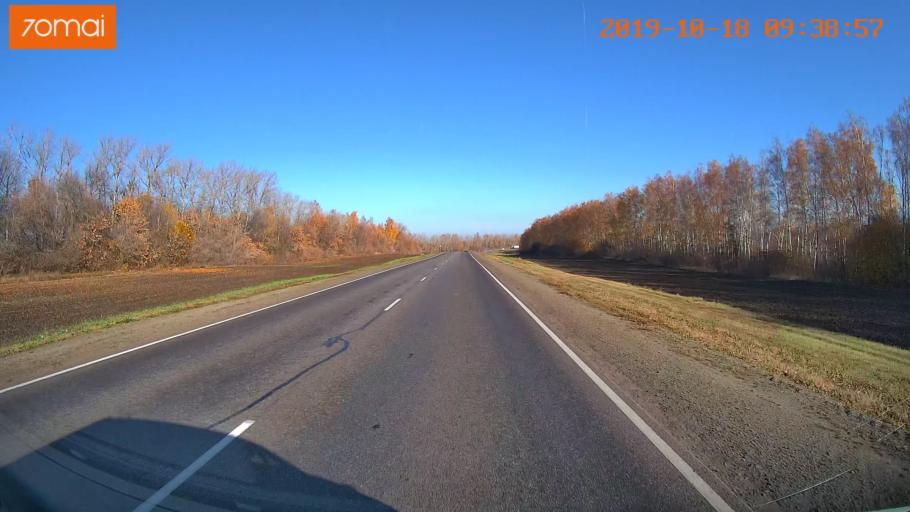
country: RU
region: Tula
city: Yefremov
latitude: 53.2458
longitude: 38.1350
